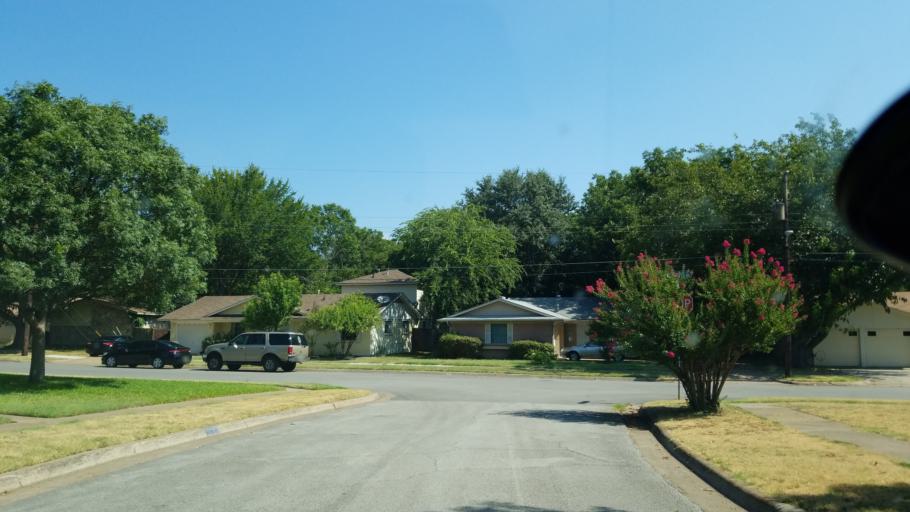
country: US
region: Texas
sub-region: Dallas County
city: Duncanville
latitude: 32.6541
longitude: -96.9042
